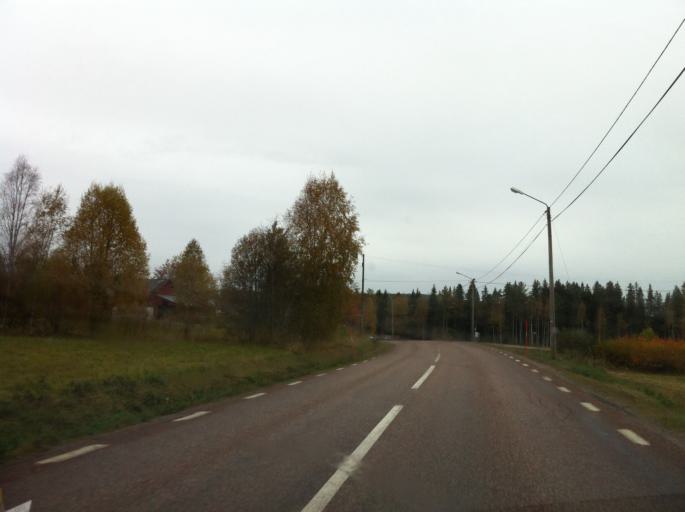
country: SE
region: Dalarna
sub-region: Ludvika Kommun
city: Grangesberg
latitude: 60.1452
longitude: 14.9879
